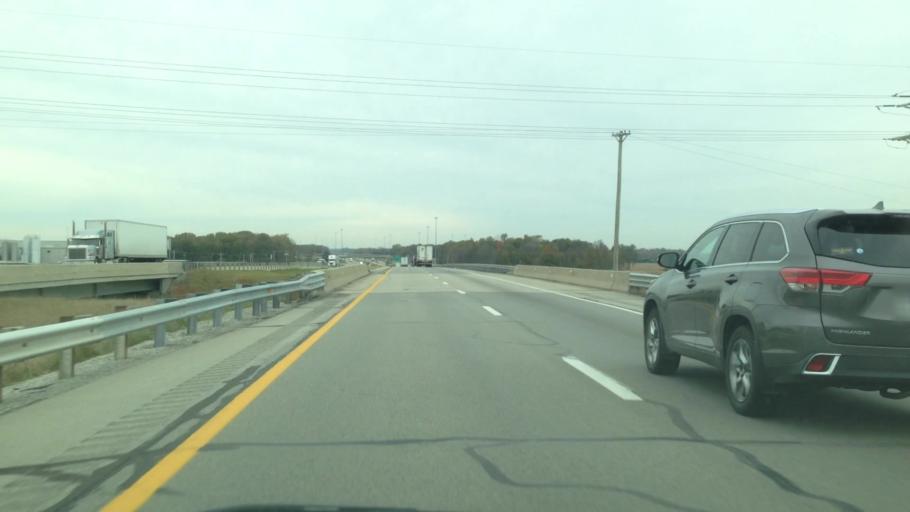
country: US
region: Ohio
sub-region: Williams County
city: Pioneer
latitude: 41.6125
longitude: -84.5357
